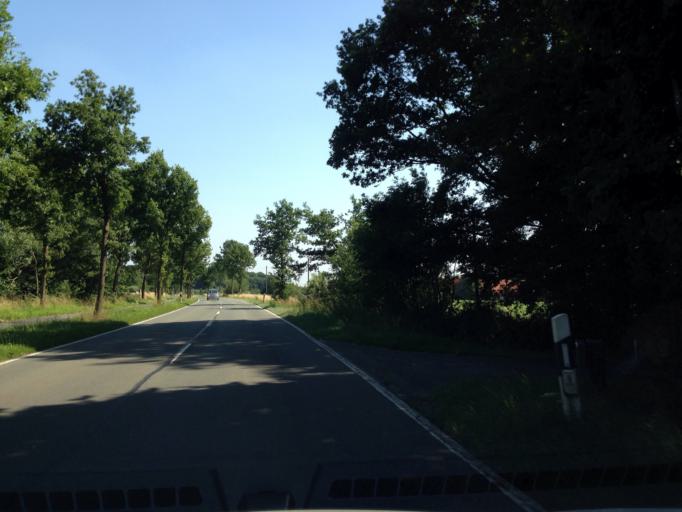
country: DE
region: North Rhine-Westphalia
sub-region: Regierungsbezirk Munster
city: Altenberge
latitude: 51.9935
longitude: 7.5293
